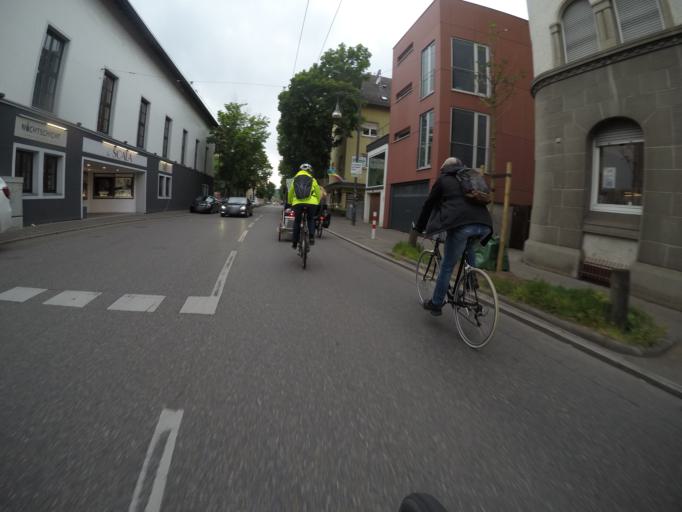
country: DE
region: Baden-Wuerttemberg
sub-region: Regierungsbezirk Stuttgart
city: Esslingen
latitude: 48.7365
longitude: 9.3156
